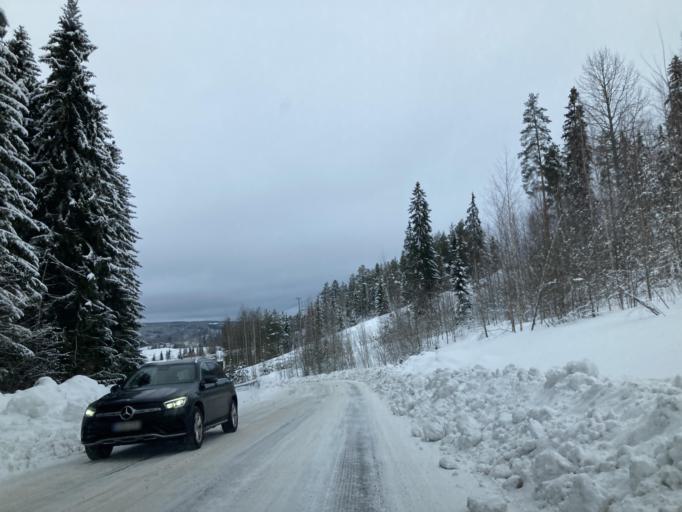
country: FI
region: Central Finland
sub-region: Jaemsae
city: Jaemsae
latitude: 61.8794
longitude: 25.3067
